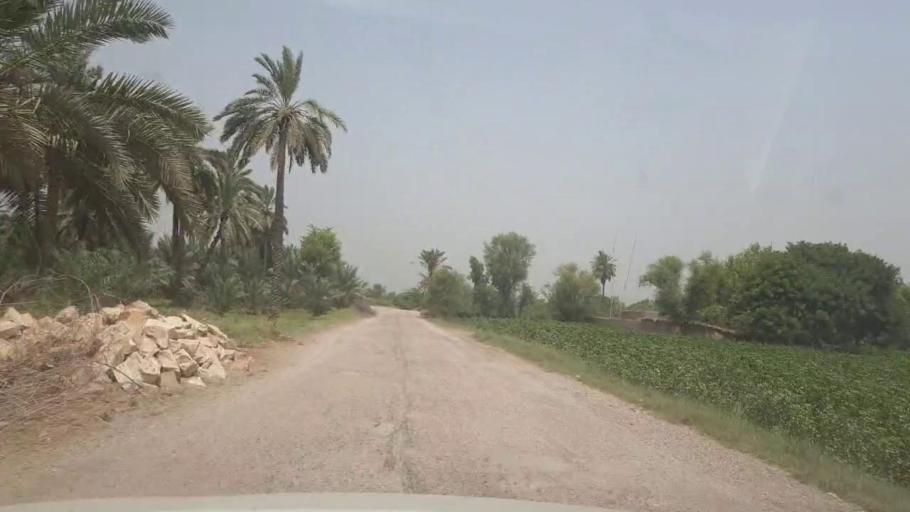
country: PK
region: Sindh
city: Kot Diji
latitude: 27.3648
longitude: 68.6586
